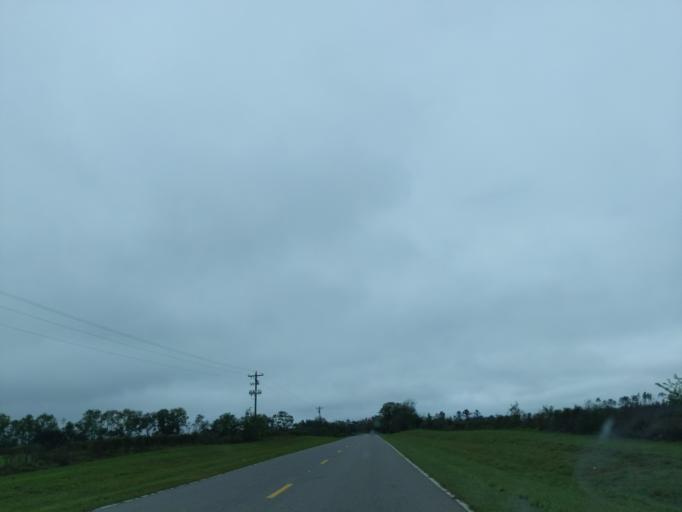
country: US
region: Florida
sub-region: Jackson County
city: Sneads
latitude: 30.6812
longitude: -84.9317
